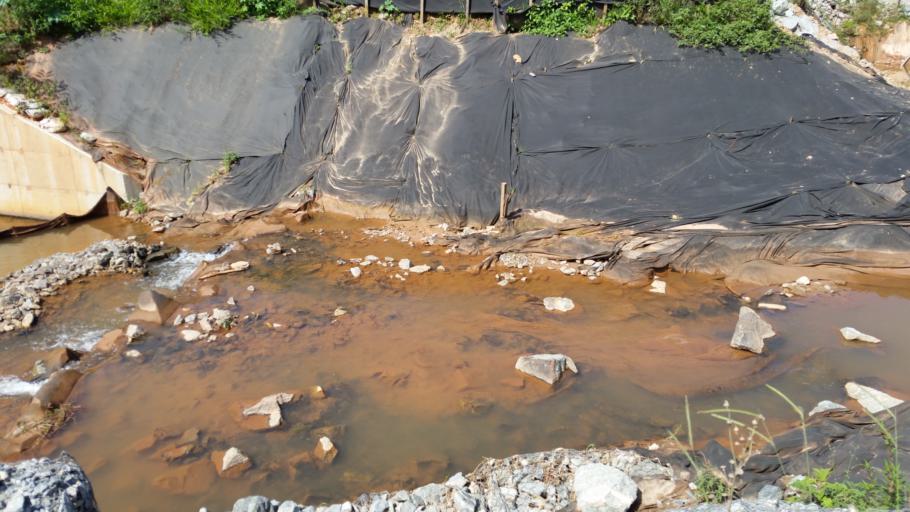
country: BR
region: Sao Paulo
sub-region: Guarulhos
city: Guarulhos
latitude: -23.4264
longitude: -46.5899
